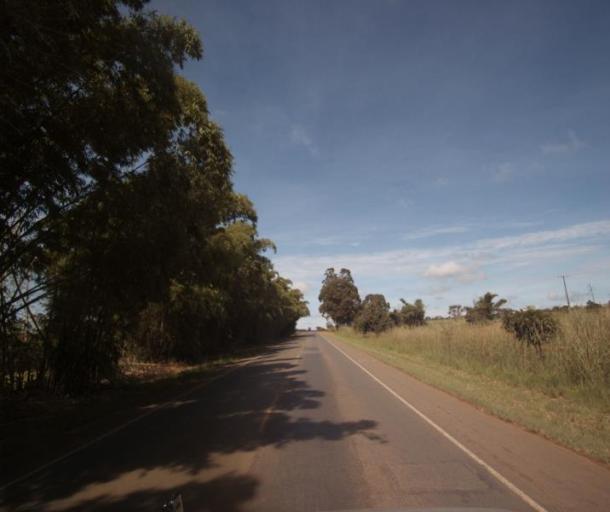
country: BR
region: Goias
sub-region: Anapolis
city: Anapolis
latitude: -16.2195
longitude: -48.9218
